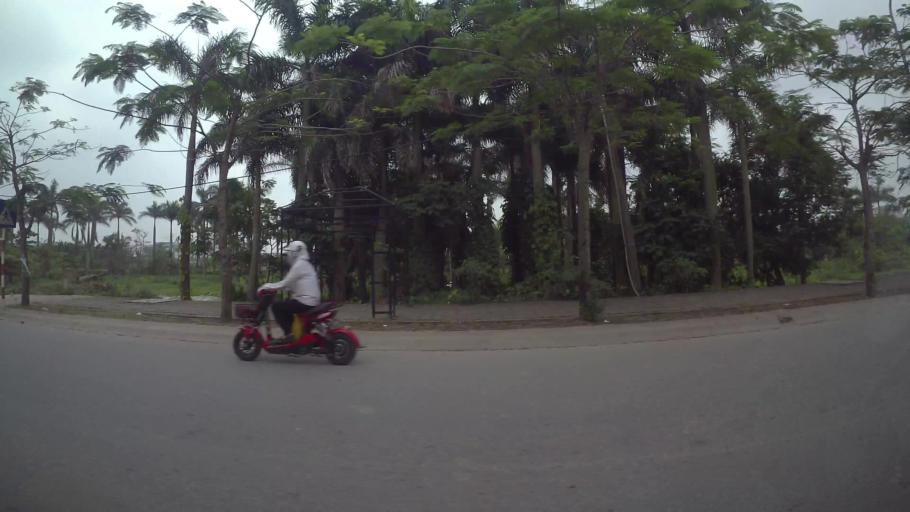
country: VN
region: Ha Noi
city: Trau Quy
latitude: 21.0566
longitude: 105.9174
